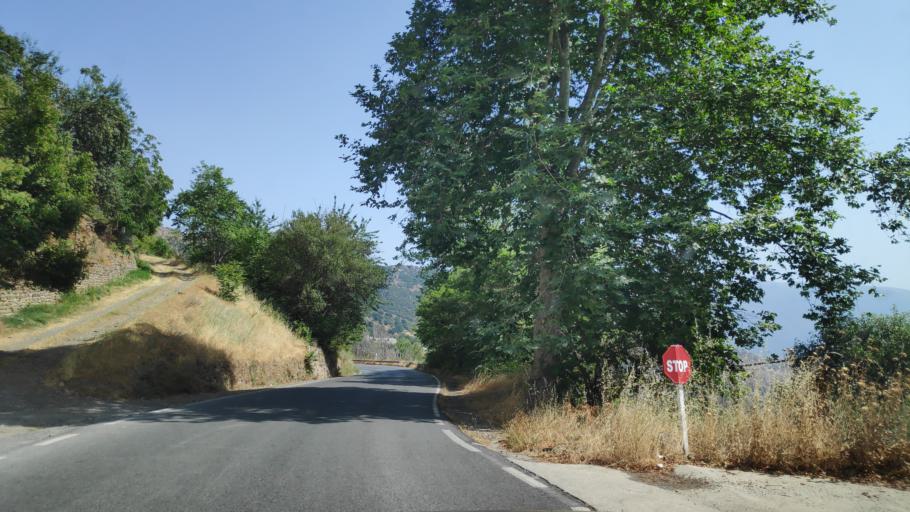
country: ES
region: Andalusia
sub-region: Provincia de Granada
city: Capileira
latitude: 36.9566
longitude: -3.3568
